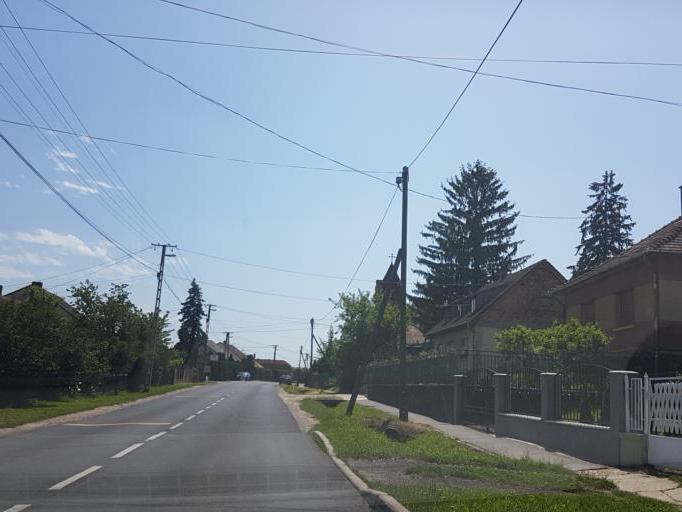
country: HU
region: Zala
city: Zalaegerszeg
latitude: 46.8532
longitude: 16.7769
